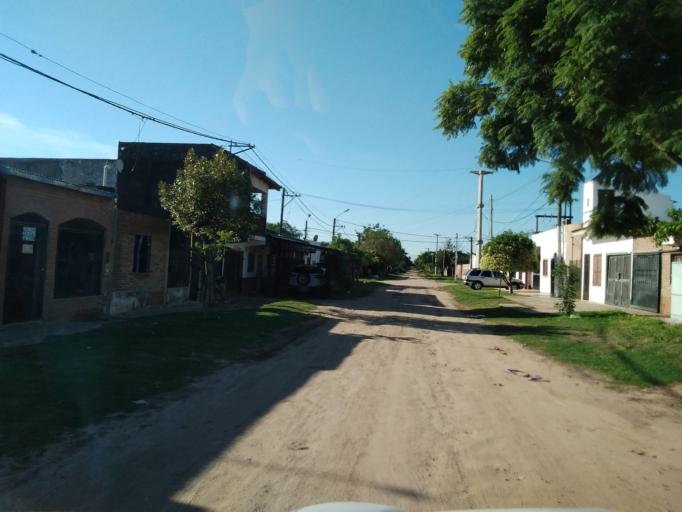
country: AR
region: Corrientes
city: Corrientes
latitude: -27.5037
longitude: -58.7837
